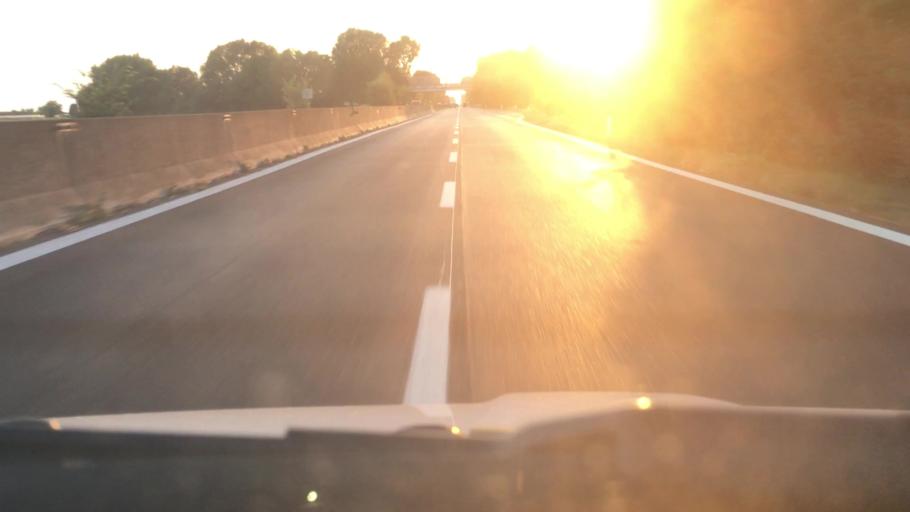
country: IT
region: Emilia-Romagna
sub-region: Provincia di Ferrara
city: Voghiera
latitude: 44.7807
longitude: 11.7720
